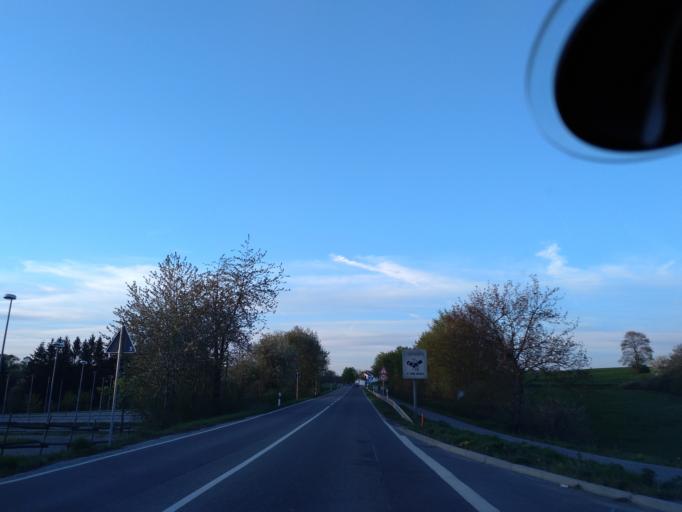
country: DE
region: Baden-Wuerttemberg
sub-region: Regierungsbezirk Stuttgart
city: Crailsheim
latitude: 49.1493
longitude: 10.0745
